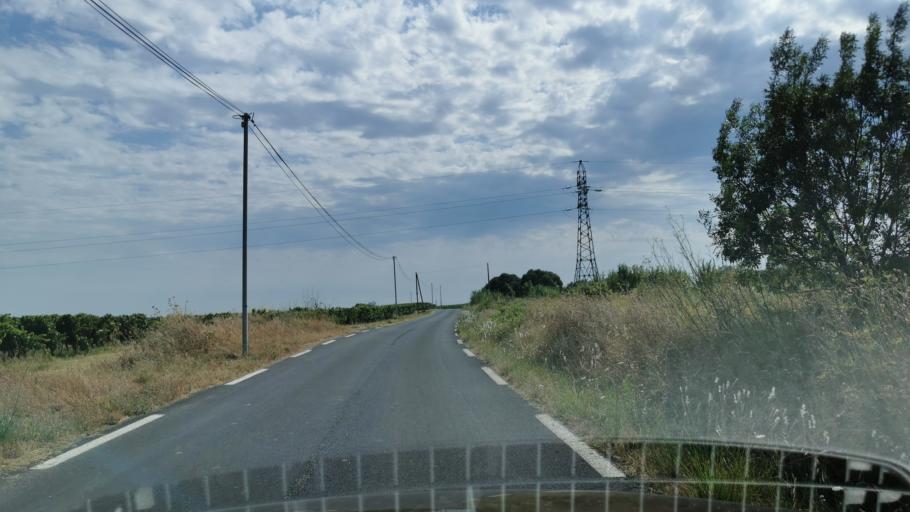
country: FR
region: Languedoc-Roussillon
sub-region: Departement de l'Herault
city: Cazouls-les-Beziers
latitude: 43.3787
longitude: 3.0992
